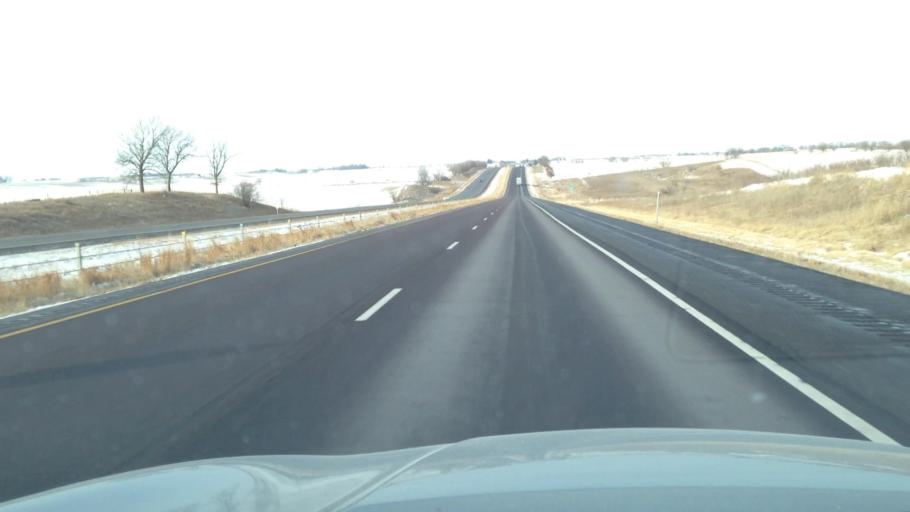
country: US
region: Iowa
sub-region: Poweshiek County
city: Grinnell
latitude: 41.6958
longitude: -92.6609
